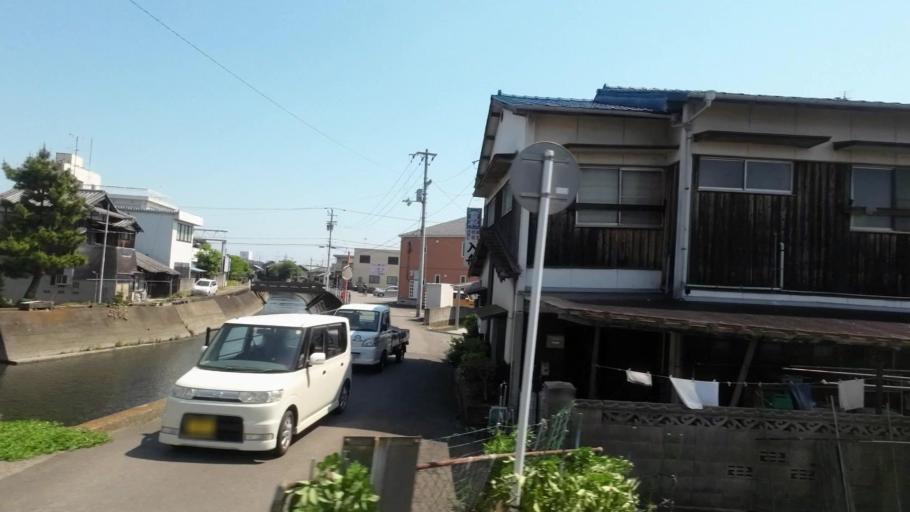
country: JP
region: Ehime
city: Saijo
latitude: 33.9314
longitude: 133.0840
